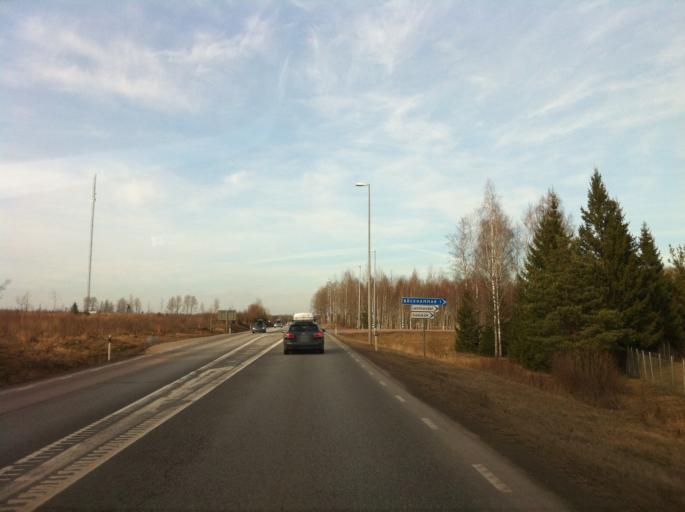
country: SE
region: Vaermland
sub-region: Kristinehamns Kommun
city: Bjorneborg
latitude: 59.1602
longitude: 14.1777
